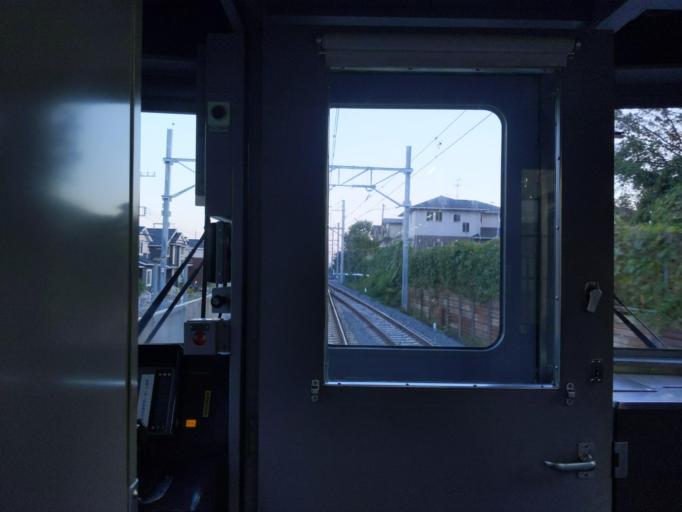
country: JP
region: Chiba
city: Noda
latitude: 35.9572
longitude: 139.8611
